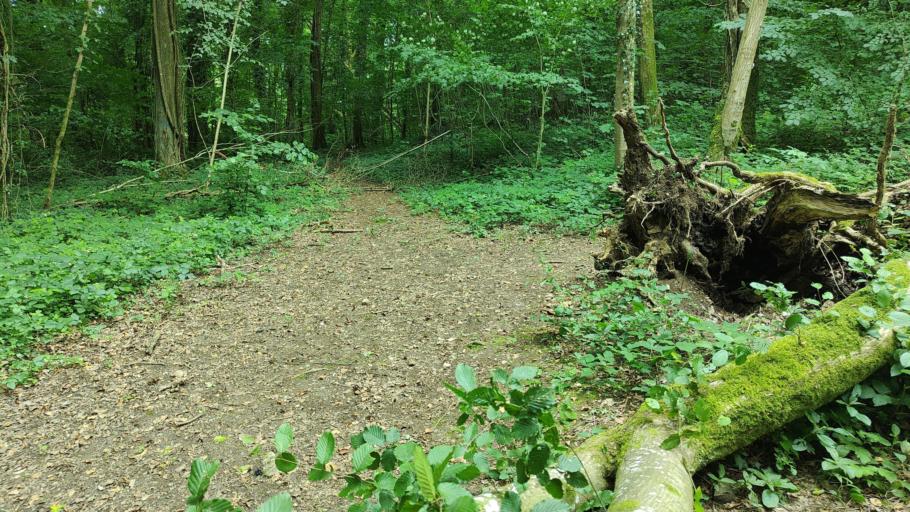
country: BE
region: Wallonia
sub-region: Province du Hainaut
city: Chimay
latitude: 50.0610
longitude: 4.3923
